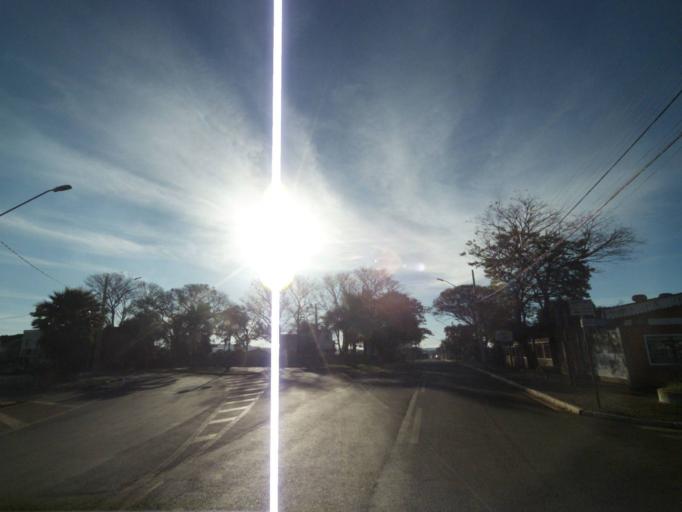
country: BR
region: Parana
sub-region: Tibagi
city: Tibagi
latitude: -24.5241
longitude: -50.4042
